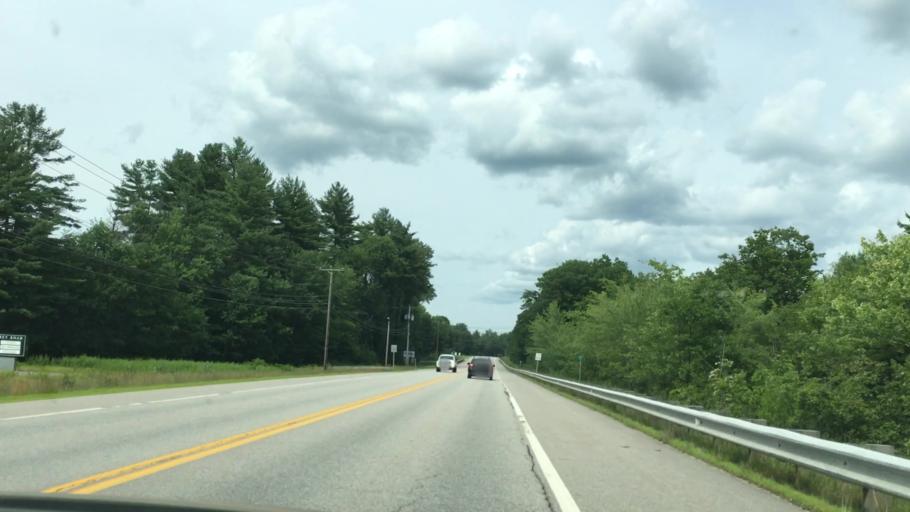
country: US
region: New Hampshire
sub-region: Hillsborough County
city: Peterborough
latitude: 42.8403
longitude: -71.9683
